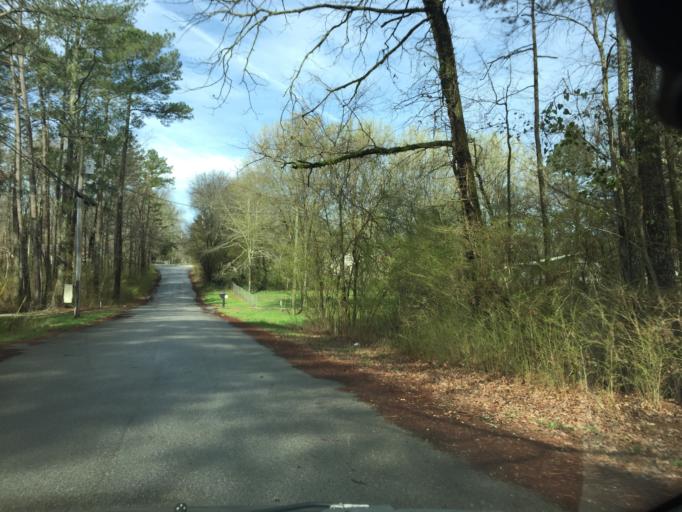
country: US
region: Tennessee
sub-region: Hamilton County
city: Collegedale
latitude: 35.0525
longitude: -85.0909
